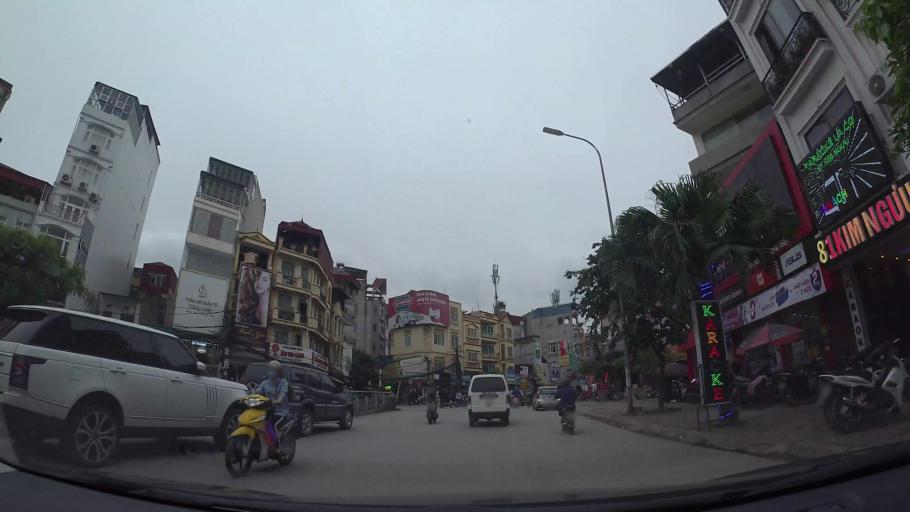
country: VN
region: Ha Noi
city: Hai BaTrung
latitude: 21.0075
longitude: 105.8611
